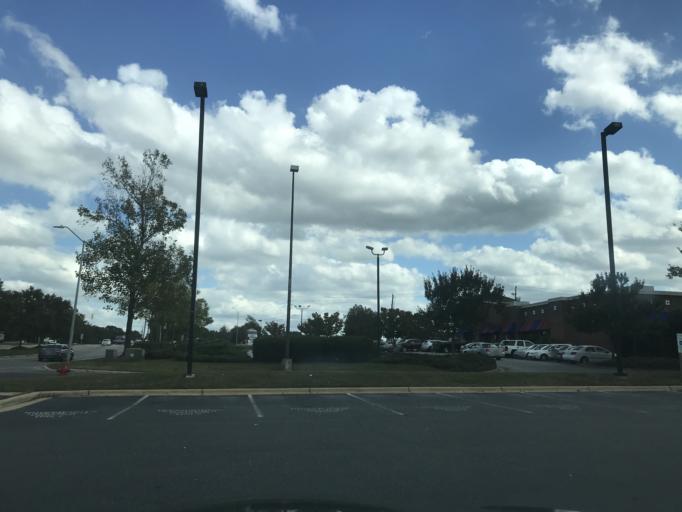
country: US
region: North Carolina
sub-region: Wake County
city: Garner
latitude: 35.7246
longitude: -78.6533
